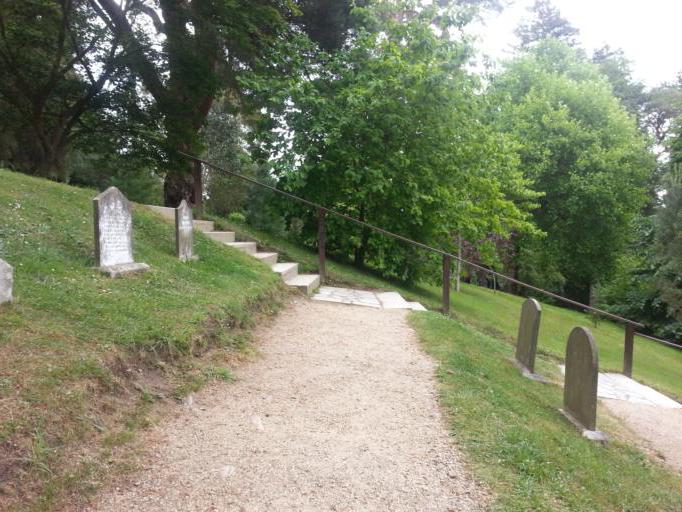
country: IE
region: Leinster
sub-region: Wicklow
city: Enniskerry
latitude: 53.1820
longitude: -6.1853
